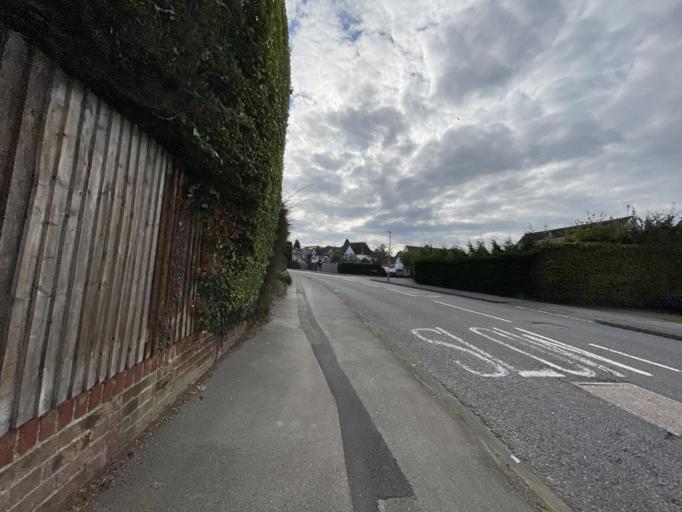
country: GB
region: England
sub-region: West Berkshire
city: Tilehurst
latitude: 51.4545
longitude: -1.0374
